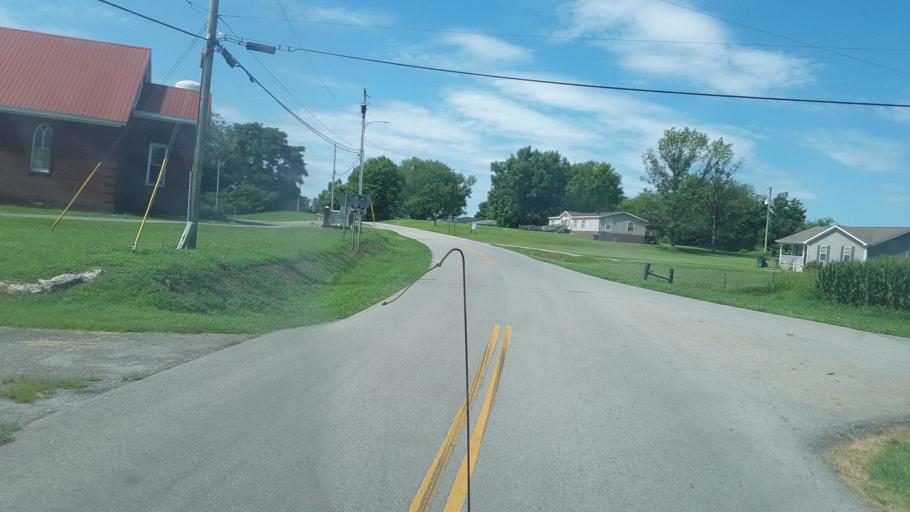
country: US
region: Kentucky
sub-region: Christian County
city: Oak Grove
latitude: 36.7819
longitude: -87.3502
